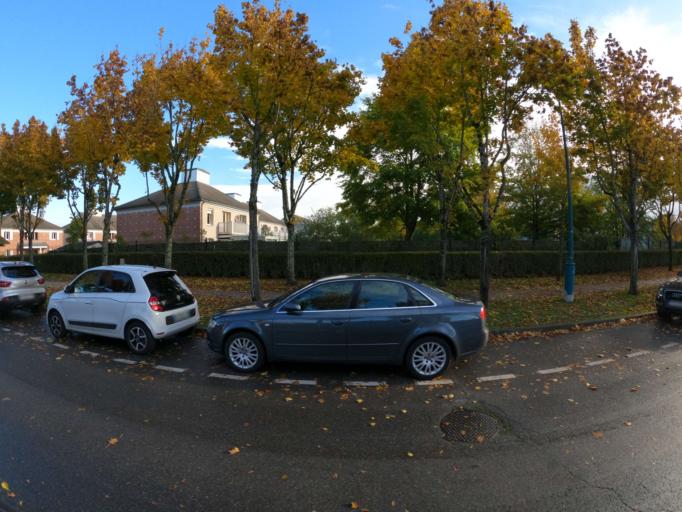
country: FR
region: Ile-de-France
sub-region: Departement de Seine-et-Marne
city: Bailly-Romainvilliers
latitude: 48.8442
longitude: 2.8176
